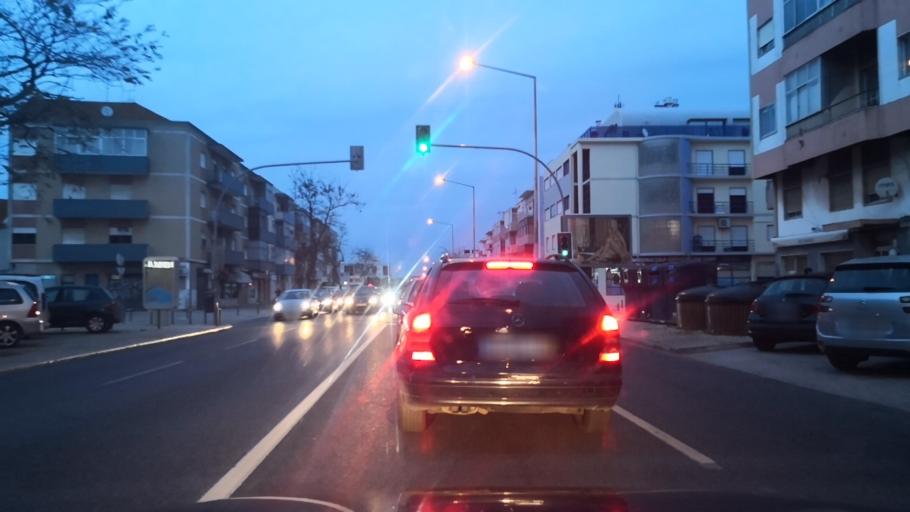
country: PT
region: Setubal
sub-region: Setubal
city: Setubal
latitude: 38.5272
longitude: -8.8752
